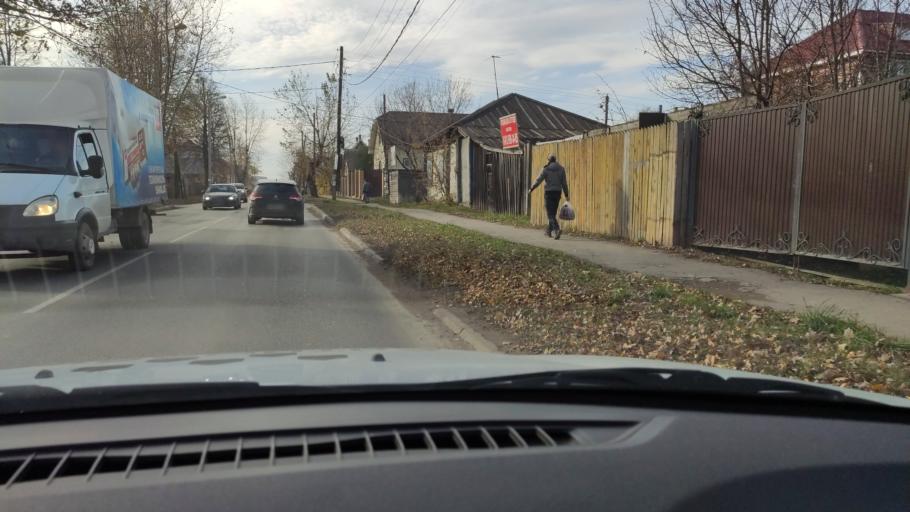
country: RU
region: Perm
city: Perm
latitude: 58.0204
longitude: 56.3157
